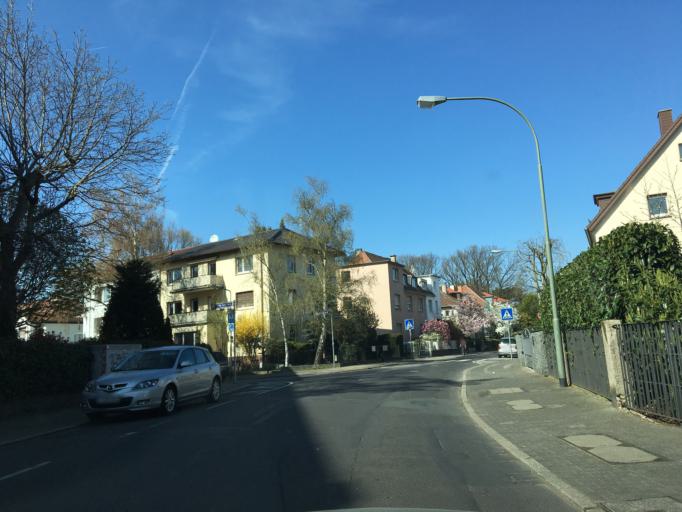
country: DE
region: Hesse
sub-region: Regierungsbezirk Darmstadt
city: Frankfurt am Main
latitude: 50.1497
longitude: 8.6564
